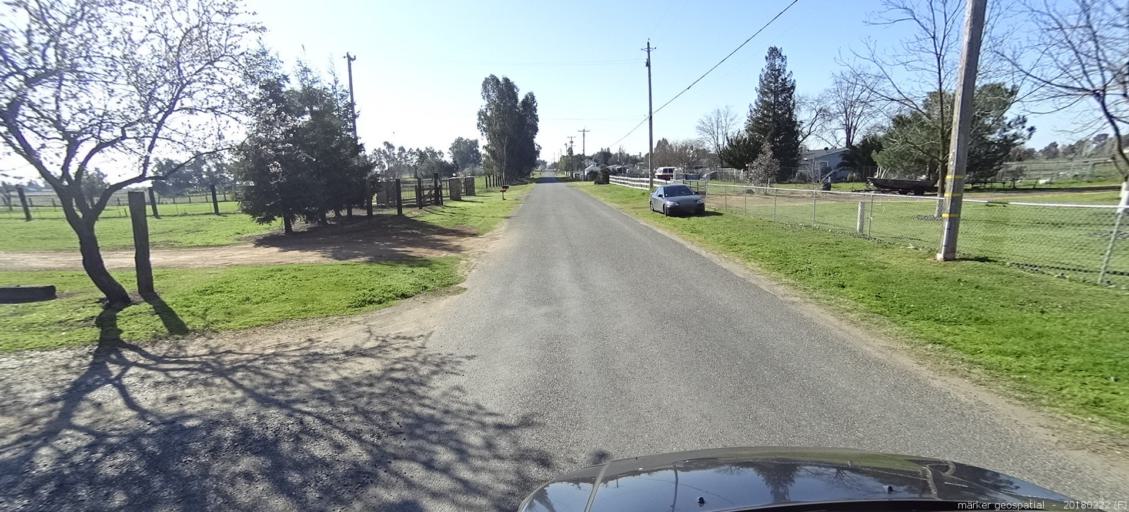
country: US
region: California
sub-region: Sacramento County
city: Elverta
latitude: 38.7345
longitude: -121.4514
